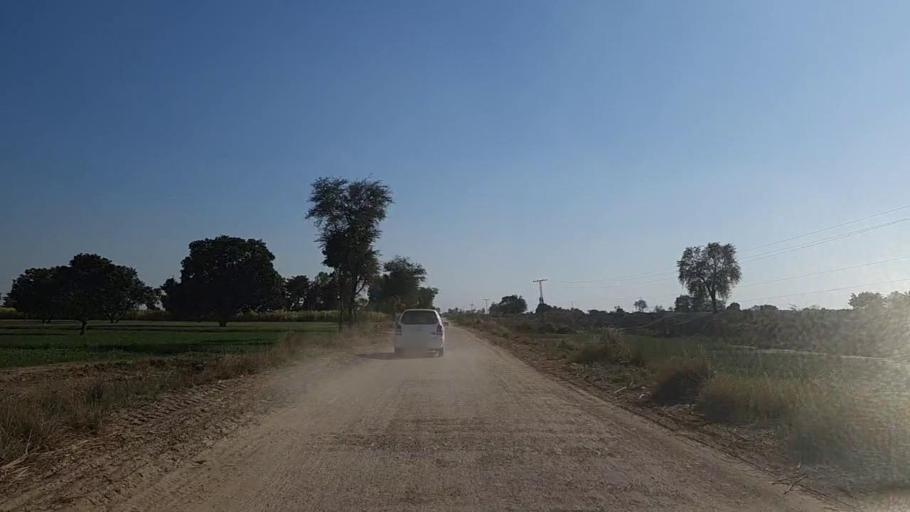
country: PK
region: Sindh
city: Nawabshah
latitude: 26.2306
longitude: 68.4272
